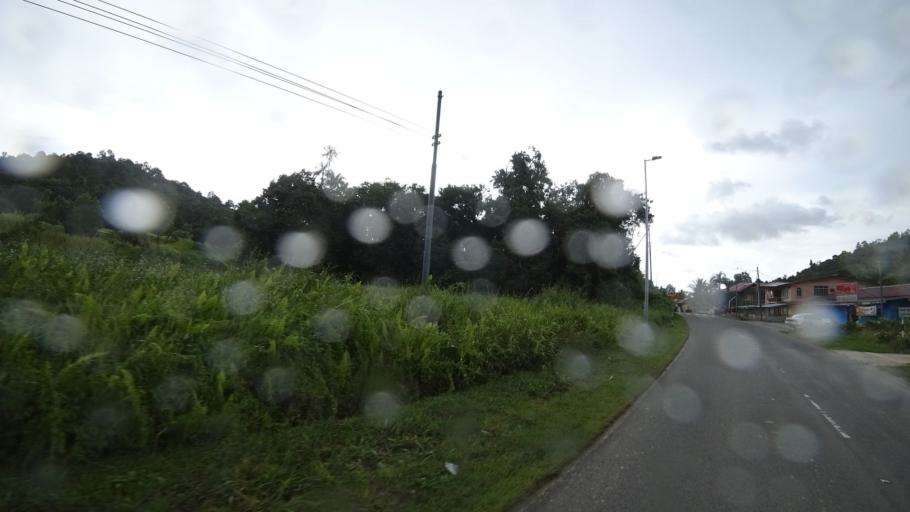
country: BN
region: Brunei and Muara
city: Bandar Seri Begawan
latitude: 4.8671
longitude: 114.9429
